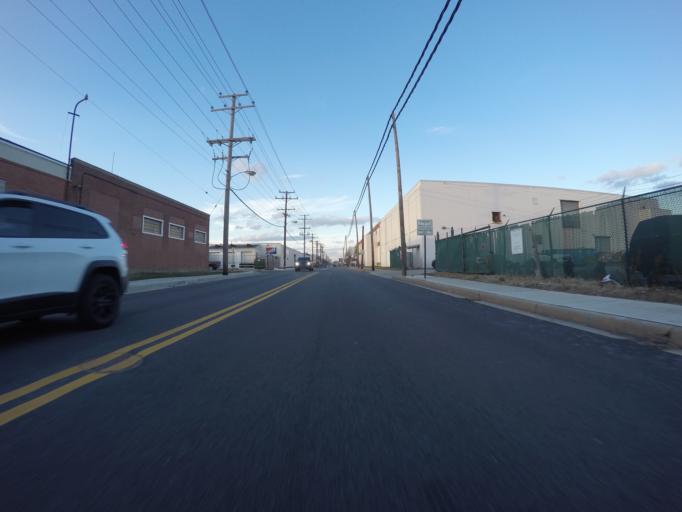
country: US
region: Maryland
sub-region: City of Baltimore
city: Baltimore
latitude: 39.2841
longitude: -76.5622
